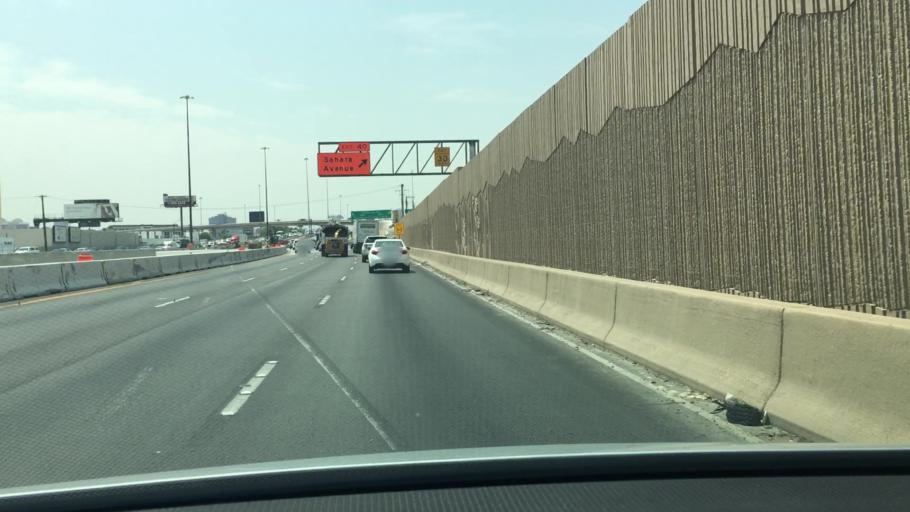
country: US
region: Nevada
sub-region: Clark County
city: Las Vegas
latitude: 36.1494
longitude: -115.1674
